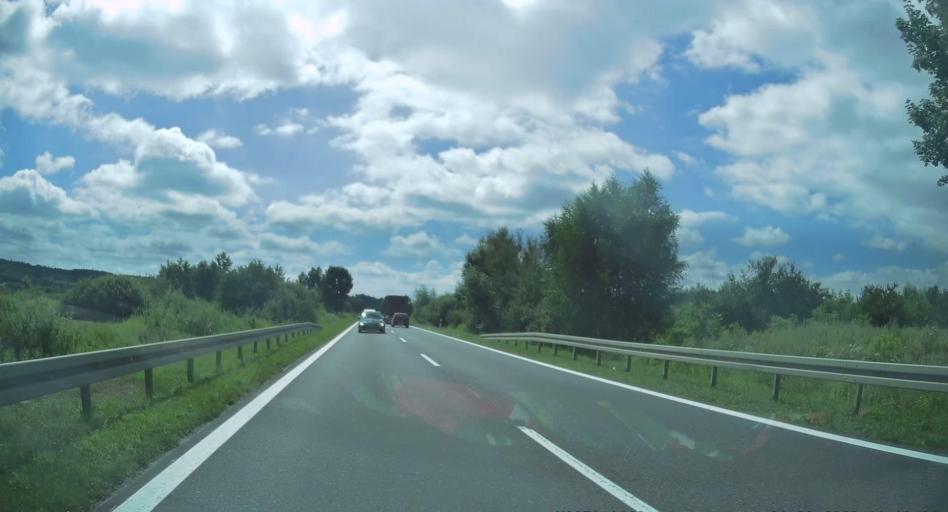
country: PL
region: Subcarpathian Voivodeship
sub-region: Powiat tarnobrzeski
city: Baranow Sandomierski
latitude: 50.4978
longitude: 21.5707
